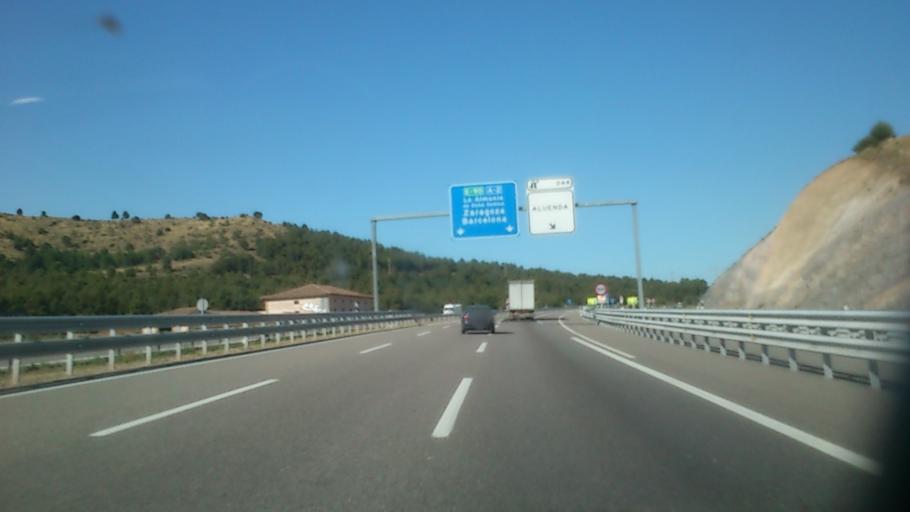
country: ES
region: Aragon
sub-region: Provincia de Zaragoza
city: Paracuellos de la Ribera
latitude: 41.3884
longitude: -1.5653
